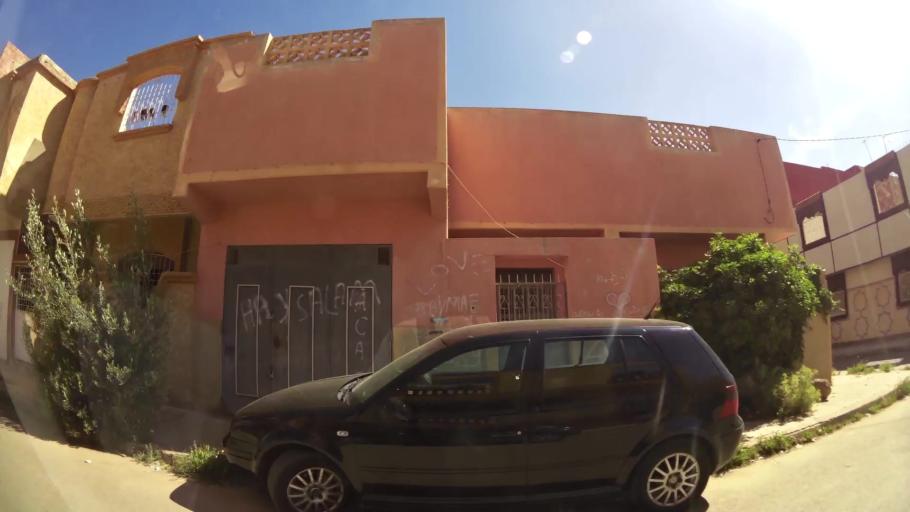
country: MA
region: Oriental
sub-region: Oujda-Angad
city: Oujda
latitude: 34.6591
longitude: -1.9309
